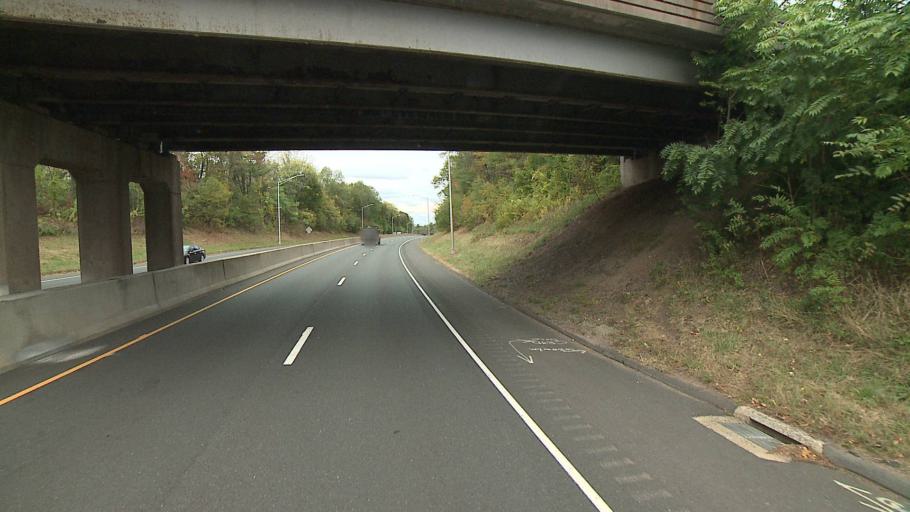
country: US
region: Connecticut
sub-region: Middlesex County
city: Middletown
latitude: 41.5471
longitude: -72.6305
